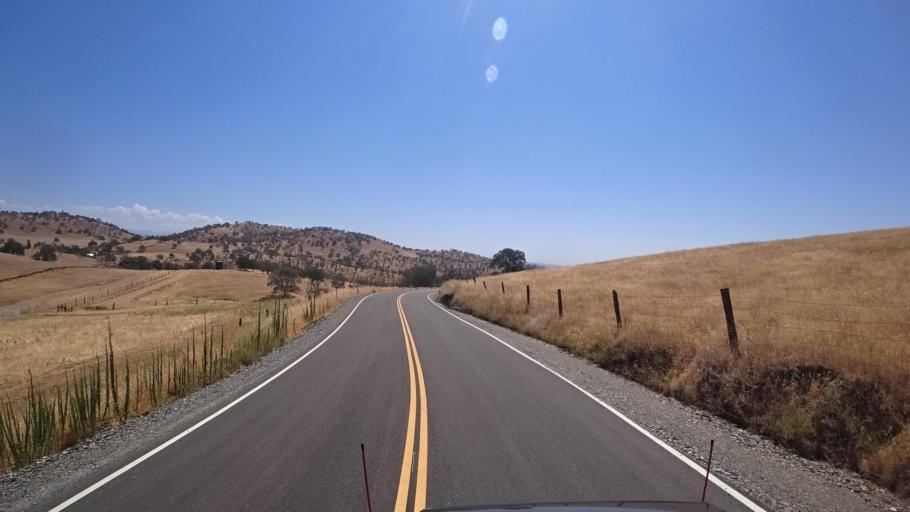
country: US
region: California
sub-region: Mariposa County
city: Mariposa
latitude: 37.3482
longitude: -119.9656
